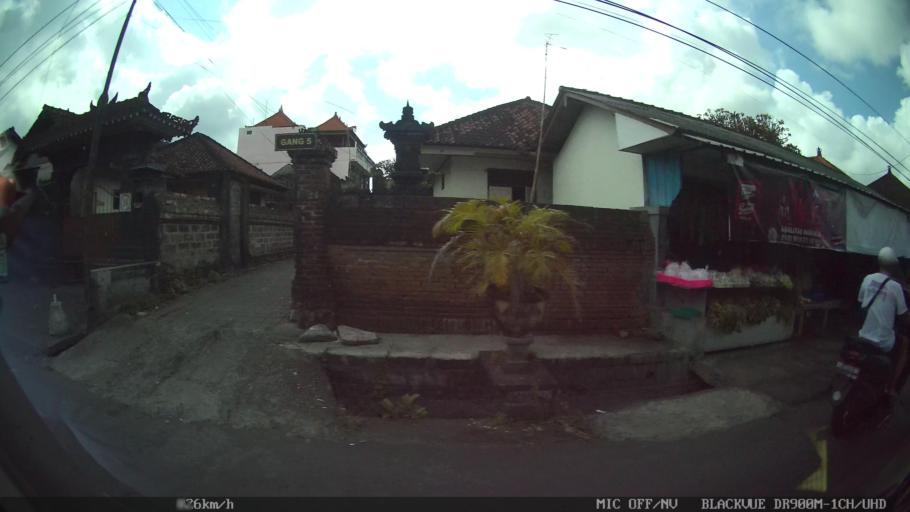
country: ID
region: Bali
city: Banjar Kertasari
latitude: -8.6190
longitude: 115.2022
